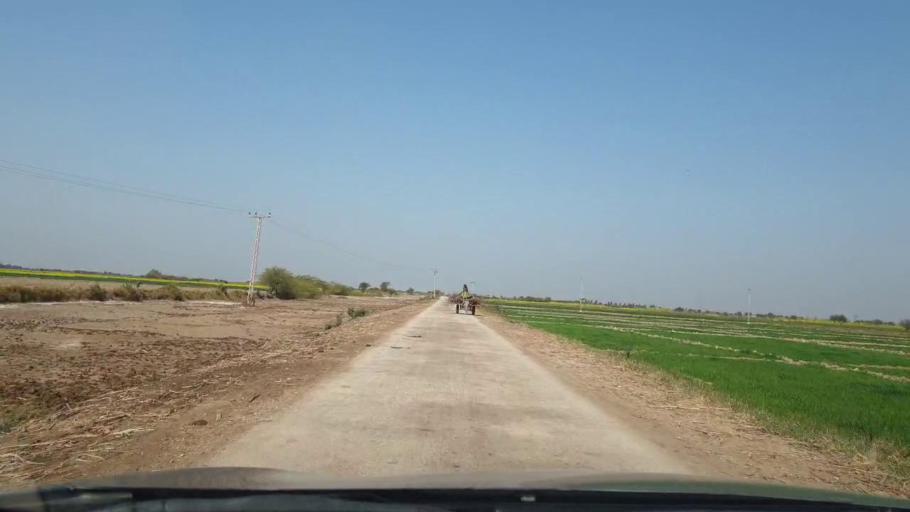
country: PK
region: Sindh
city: Mirpur Khas
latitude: 25.5970
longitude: 68.8891
